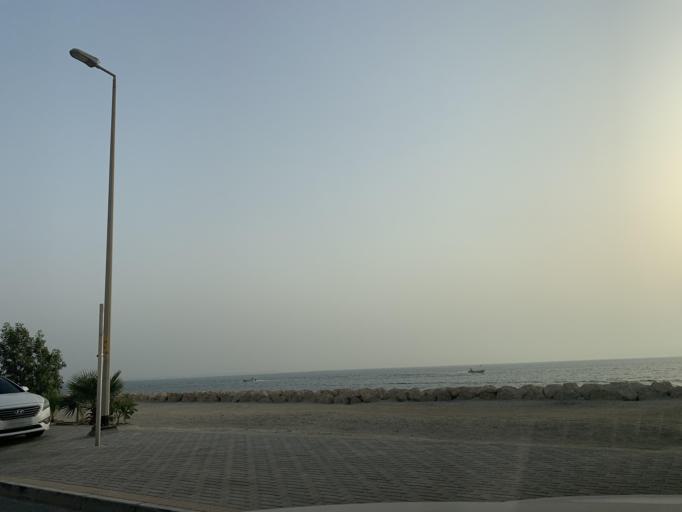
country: BH
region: Manama
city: Jidd Hafs
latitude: 26.2220
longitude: 50.4382
